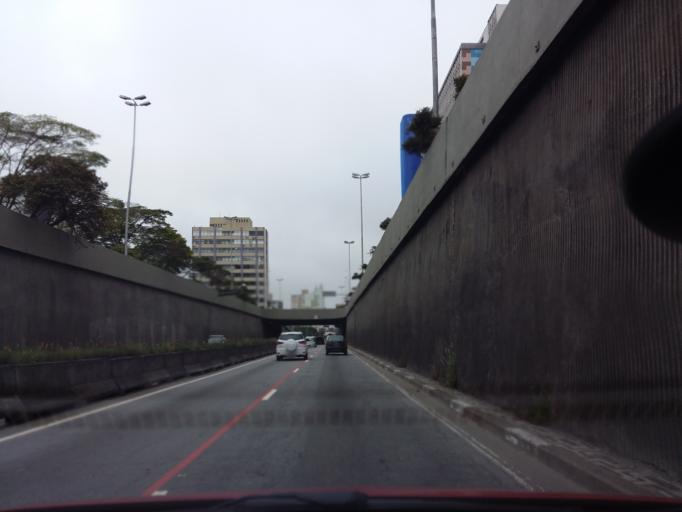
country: BR
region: Sao Paulo
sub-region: Santo Andre
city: Santo Andre
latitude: -23.6585
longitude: -46.5326
